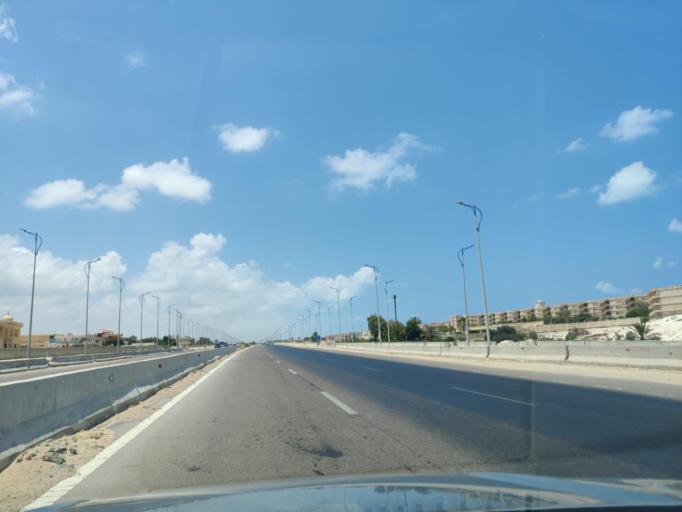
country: EG
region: Muhafazat Matruh
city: Al `Alamayn
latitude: 30.9283
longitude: 29.4726
